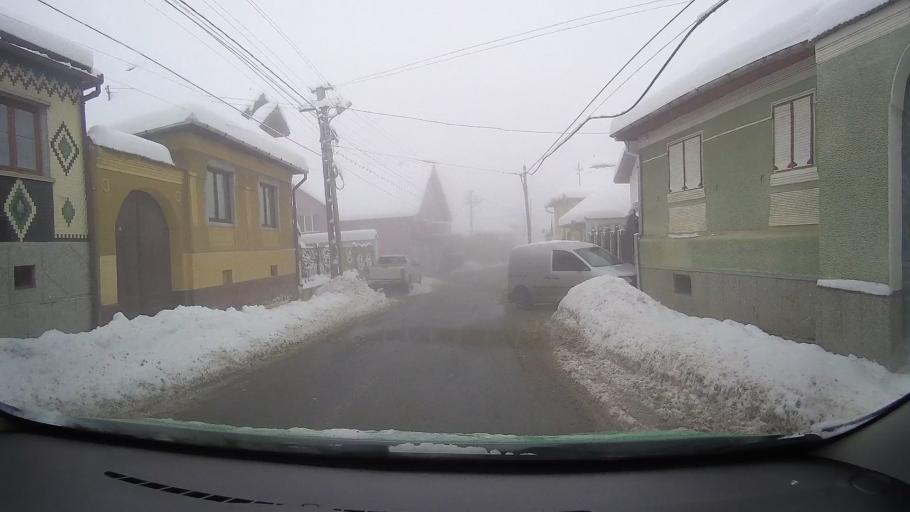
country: RO
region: Sibiu
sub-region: Comuna Jina
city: Jina
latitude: 45.7848
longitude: 23.6756
